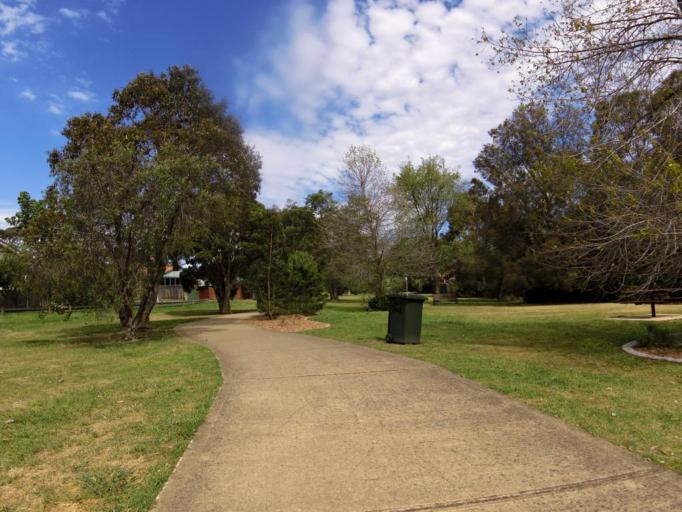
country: AU
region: Victoria
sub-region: Glen Eira
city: Murrumbeena
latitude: -37.8889
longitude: 145.0738
